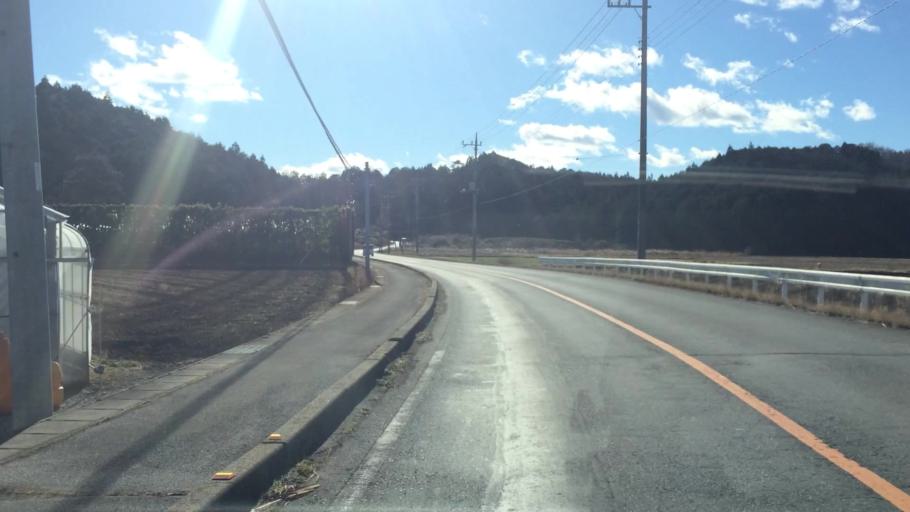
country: JP
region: Tochigi
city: Imaichi
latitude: 36.7362
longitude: 139.7472
